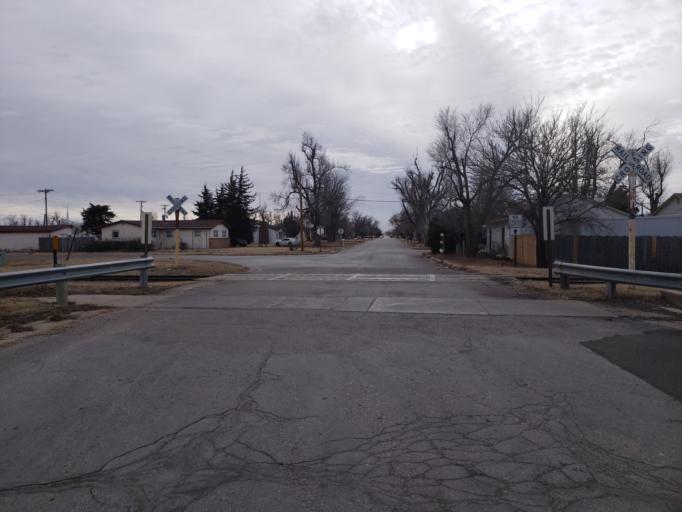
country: US
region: Kansas
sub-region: Ford County
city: Dodge City
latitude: 37.7422
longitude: -100.0148
